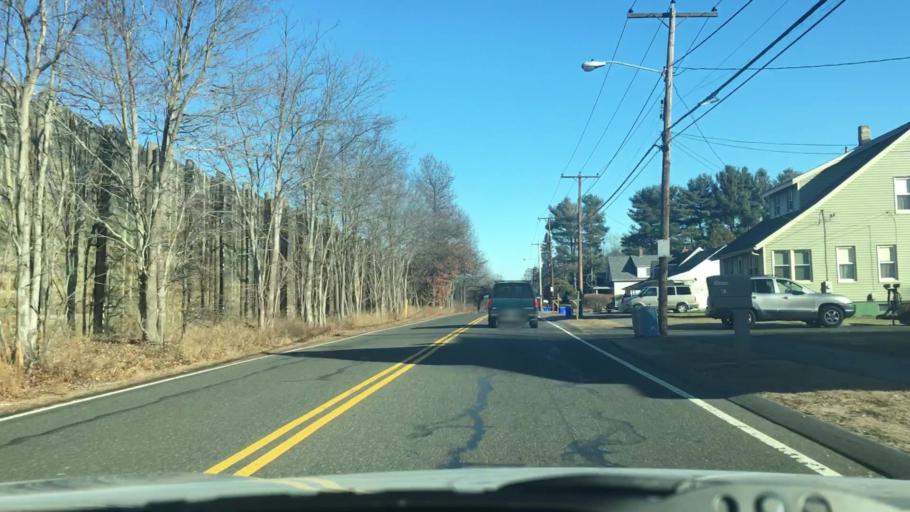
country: US
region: Massachusetts
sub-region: Hampden County
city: Ludlow
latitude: 42.1641
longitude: -72.5076
